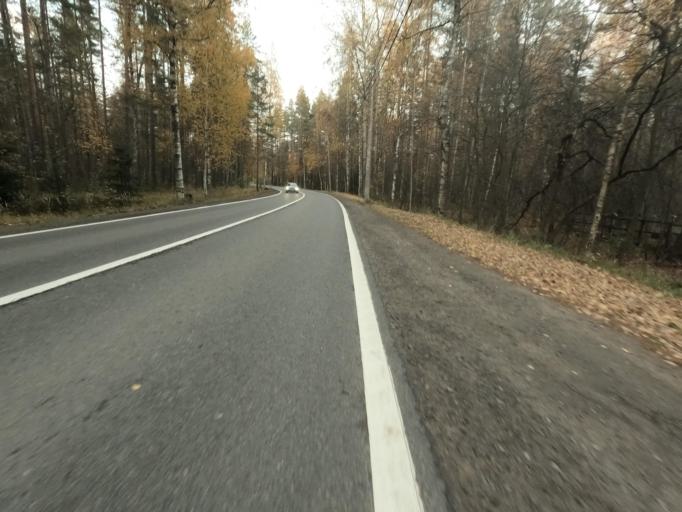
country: RU
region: St.-Petersburg
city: Repino
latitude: 60.1865
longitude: 29.8635
